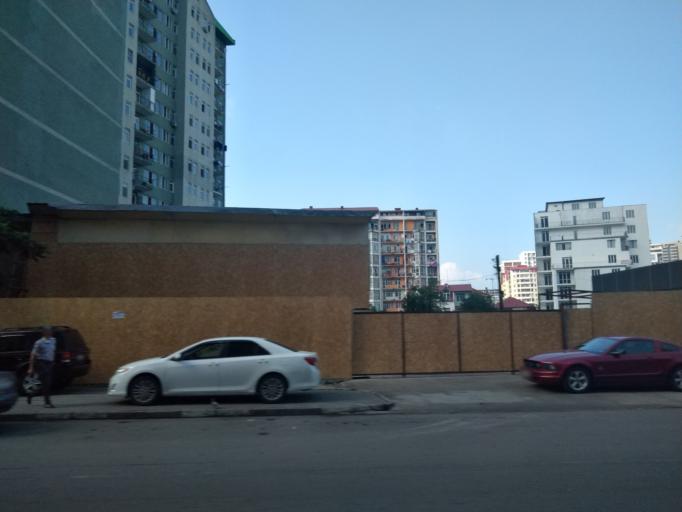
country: GE
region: Ajaria
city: Batumi
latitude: 41.6331
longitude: 41.6114
